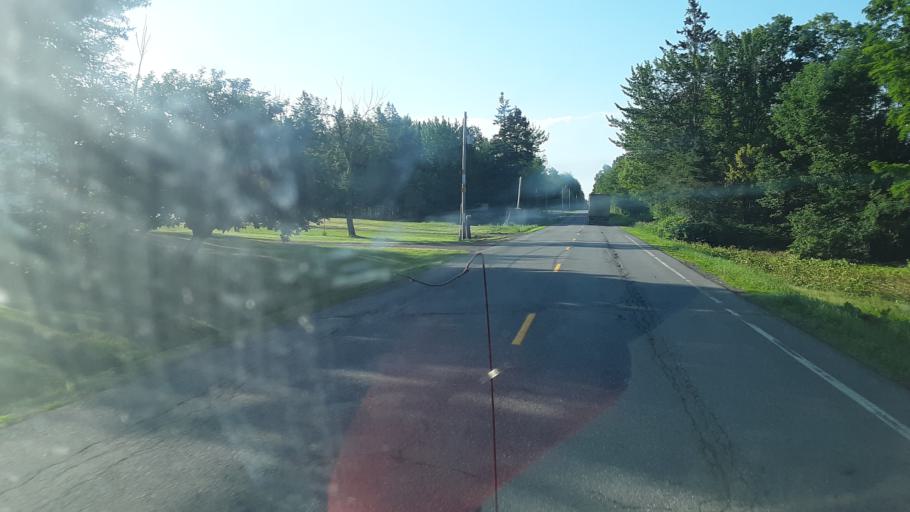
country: US
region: Maine
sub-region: Penobscot County
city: Patten
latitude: 46.1849
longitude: -68.2521
